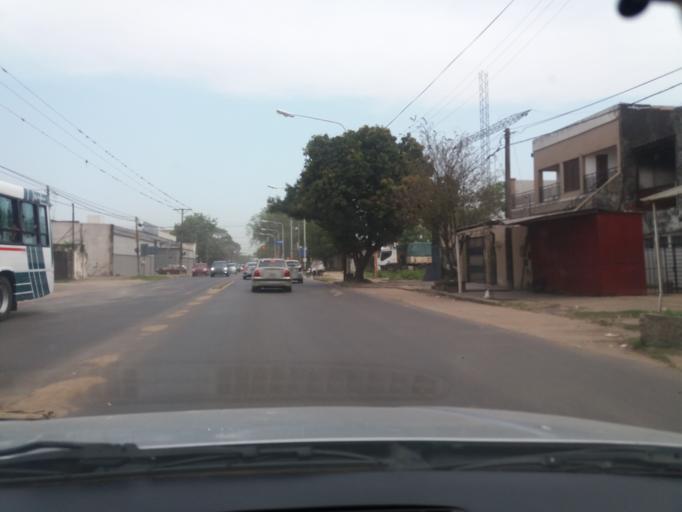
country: AR
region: Corrientes
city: Corrientes
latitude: -27.4960
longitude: -58.8167
